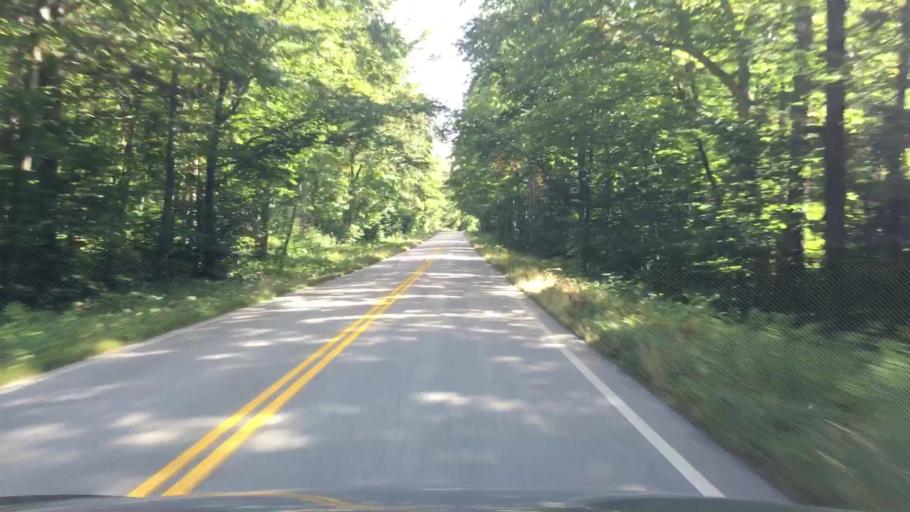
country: US
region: New Hampshire
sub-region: Carroll County
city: Tamworth
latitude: 44.0199
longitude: -71.3205
